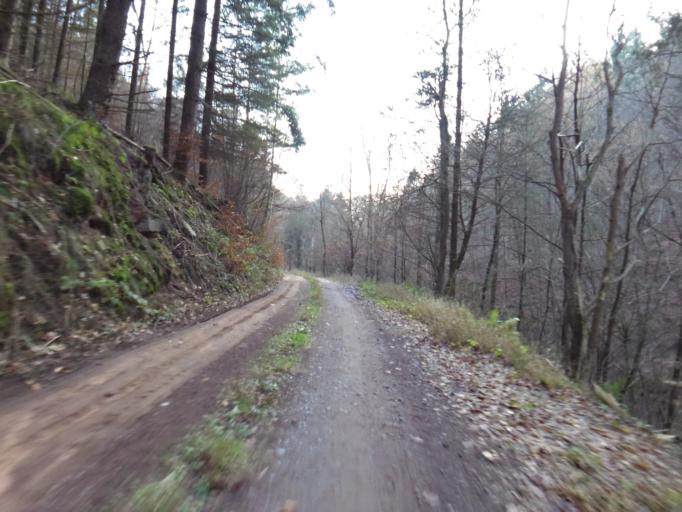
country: DE
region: Rheinland-Pfalz
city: Altleiningen
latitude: 49.4735
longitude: 8.1073
